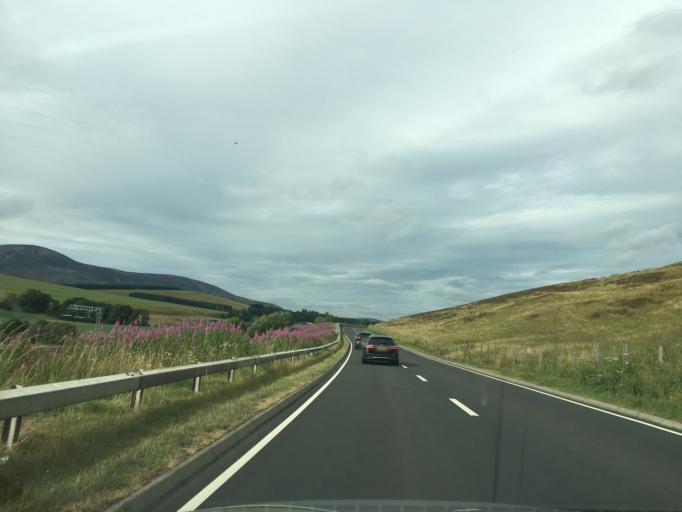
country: GB
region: Scotland
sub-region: South Lanarkshire
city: Biggar
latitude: 55.5405
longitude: -3.6599
